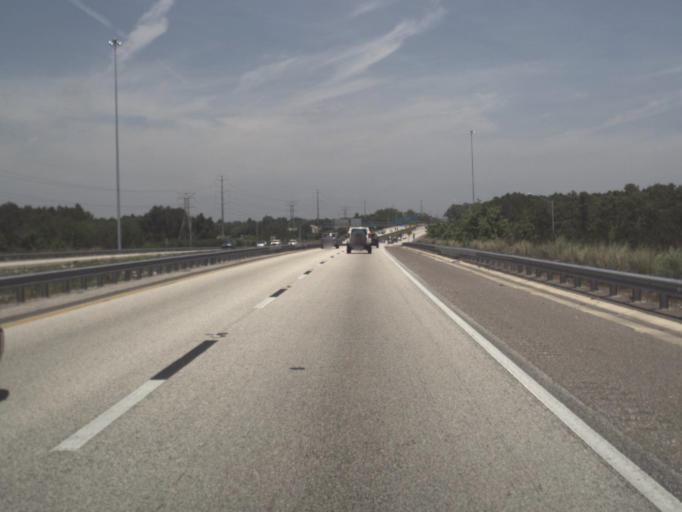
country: US
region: Florida
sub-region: Duval County
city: Jacksonville Beach
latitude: 30.2695
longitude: -81.5205
